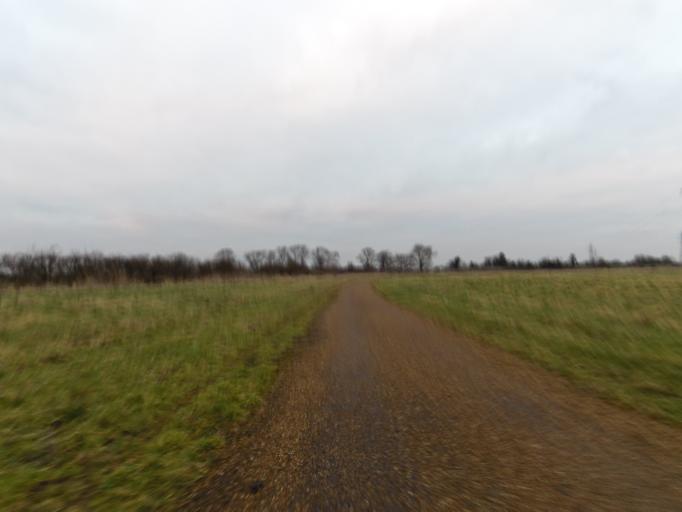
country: GB
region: England
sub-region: Cambridgeshire
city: Bottisham
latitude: 52.2630
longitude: 0.2510
